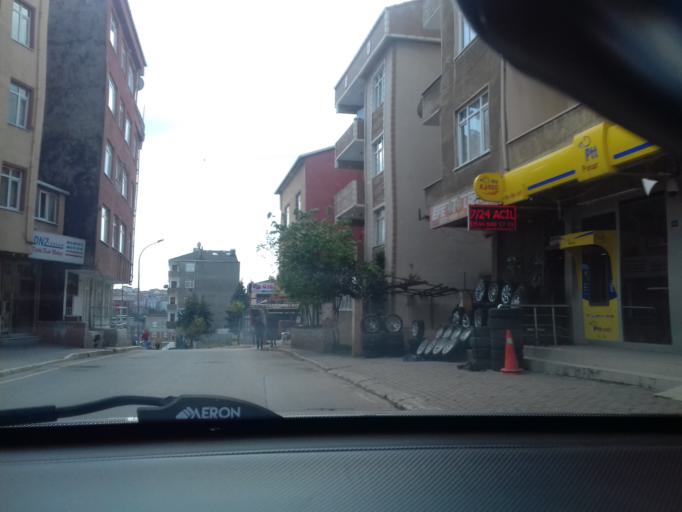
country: TR
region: Istanbul
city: Pendik
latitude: 40.8716
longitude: 29.2807
